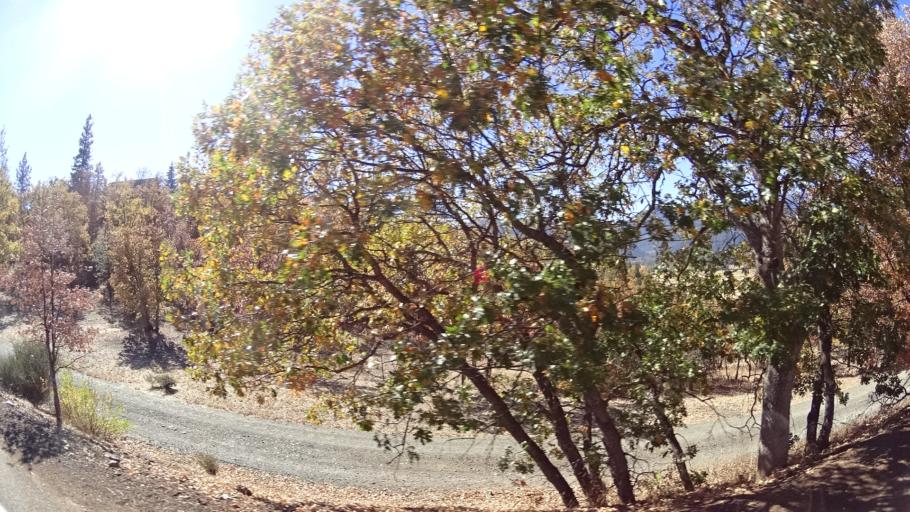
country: US
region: California
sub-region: Siskiyou County
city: Yreka
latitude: 41.5673
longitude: -122.9381
